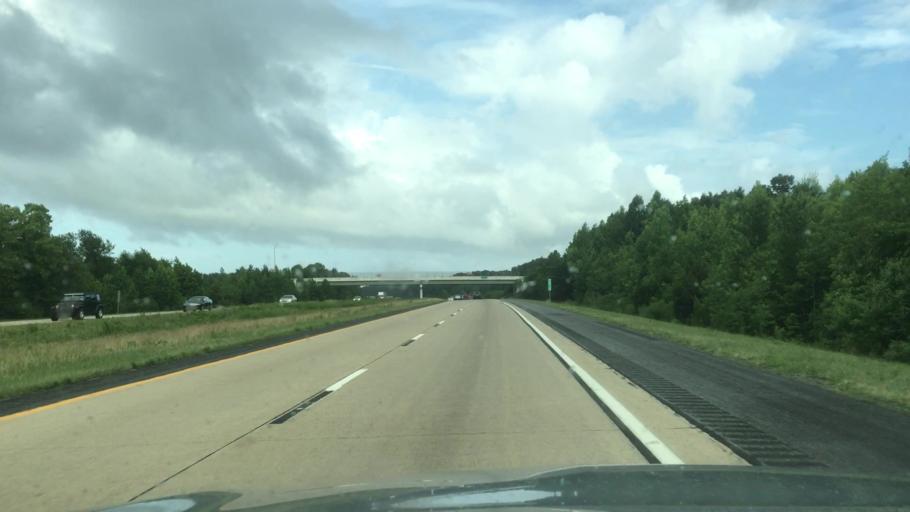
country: US
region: Delaware
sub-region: Kent County
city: Cheswold
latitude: 39.2291
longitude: -75.5749
